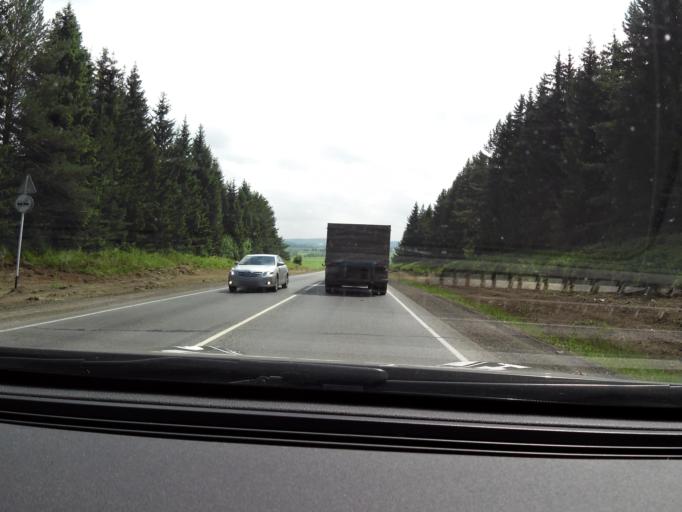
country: RU
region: Perm
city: Kukushtan
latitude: 57.5252
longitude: 56.6232
